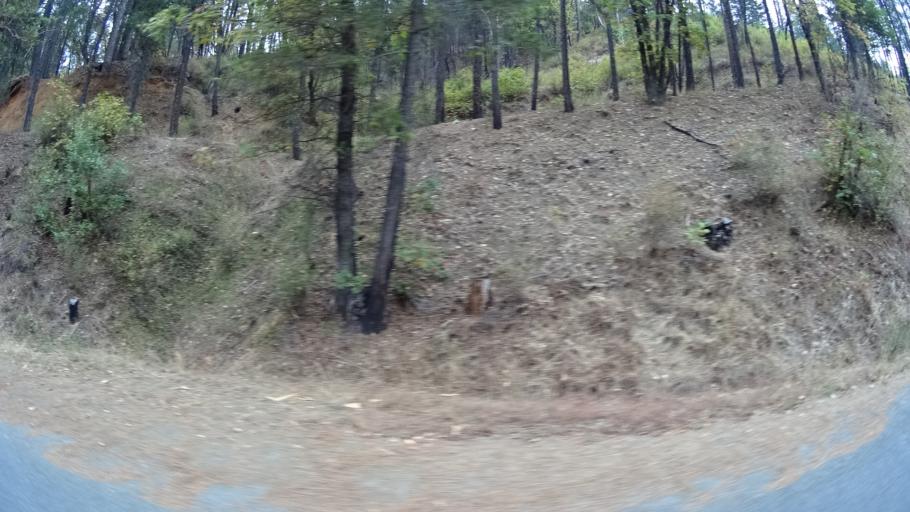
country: US
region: California
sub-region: Siskiyou County
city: Happy Camp
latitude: 41.7811
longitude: -123.3873
